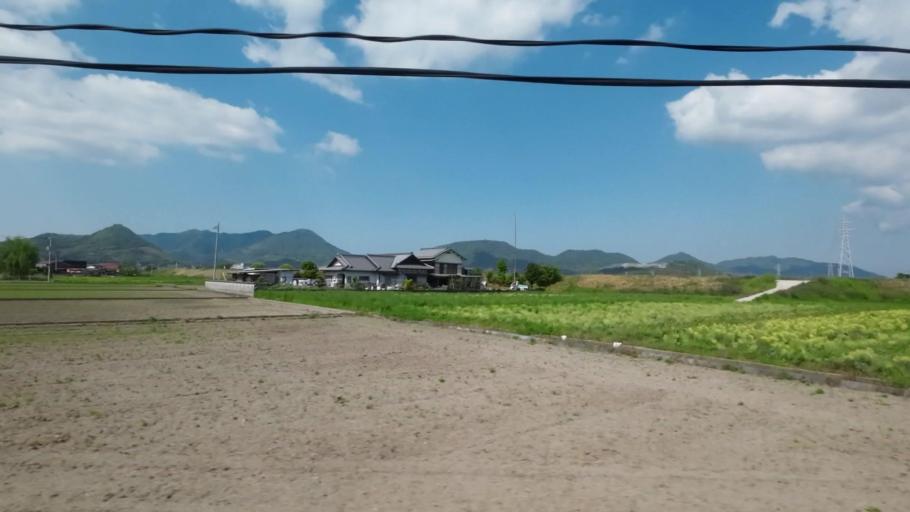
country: JP
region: Kagawa
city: Tadotsu
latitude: 34.2081
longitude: 133.7096
